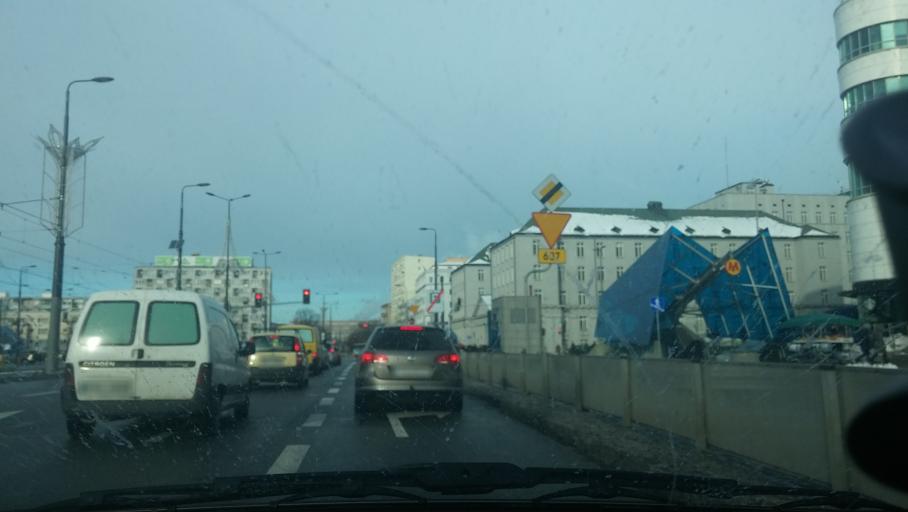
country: PL
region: Masovian Voivodeship
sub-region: Warszawa
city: Praga Polnoc
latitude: 52.2541
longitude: 21.0358
